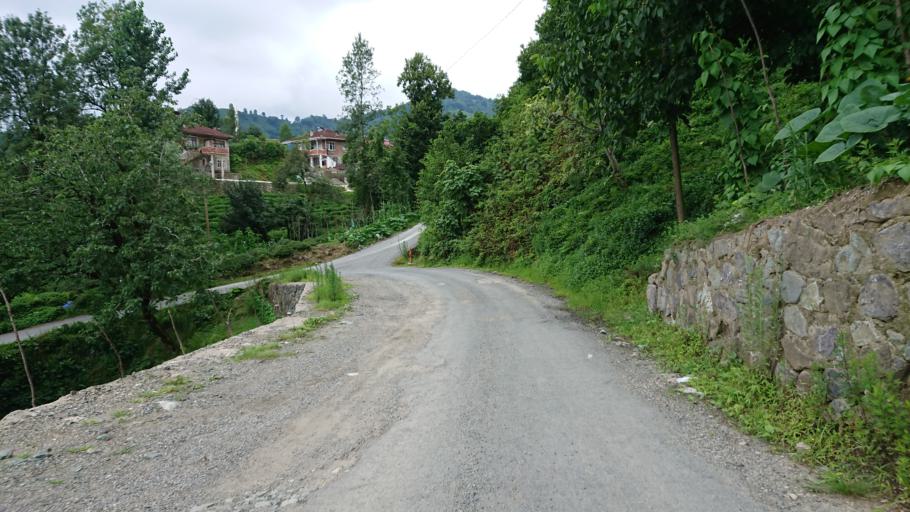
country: TR
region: Rize
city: Rize
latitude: 40.9664
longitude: 40.5109
